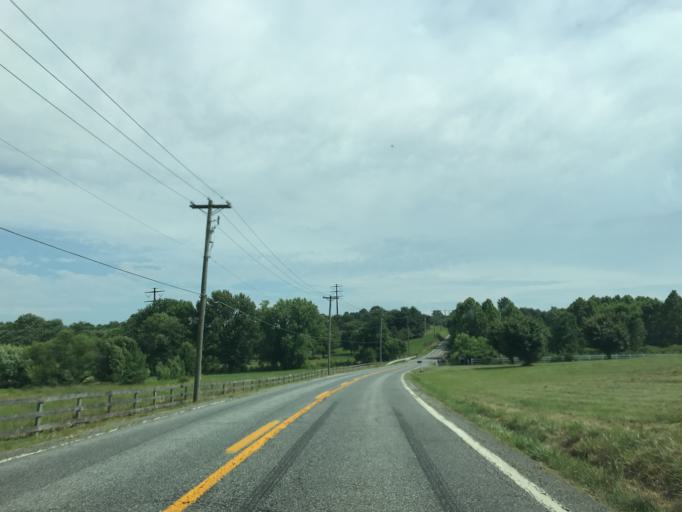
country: US
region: Pennsylvania
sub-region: York County
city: Susquehanna Trails
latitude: 39.6861
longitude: -76.3893
